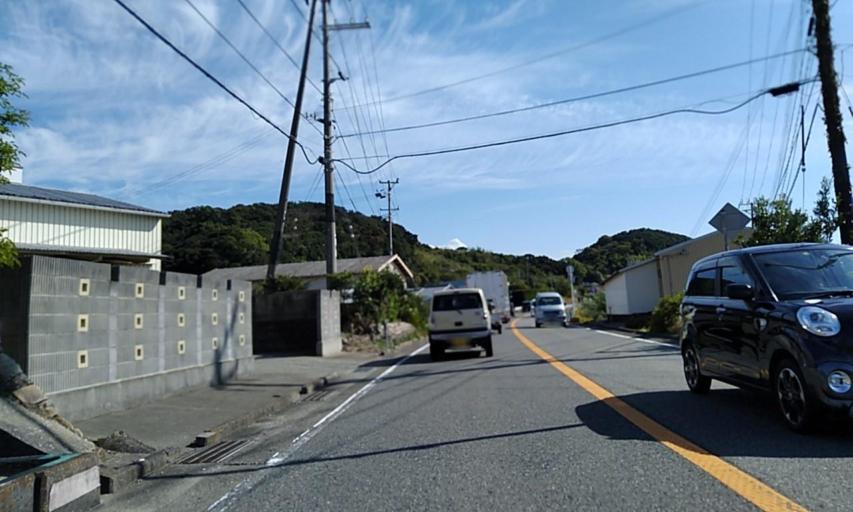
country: JP
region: Wakayama
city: Gobo
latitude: 33.8546
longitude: 135.1656
